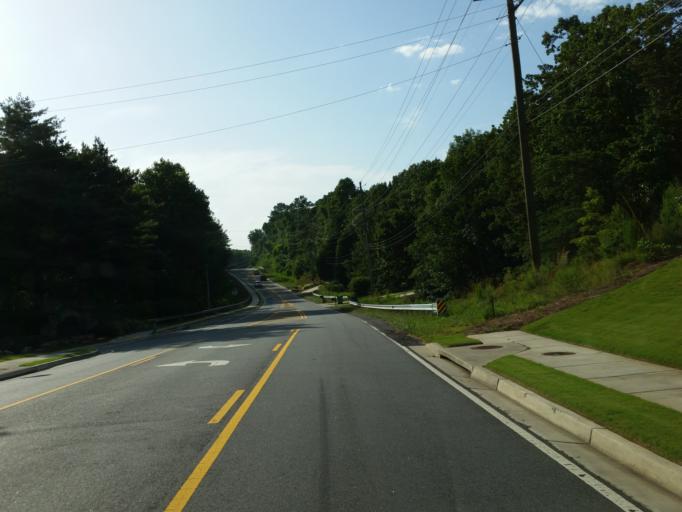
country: US
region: Georgia
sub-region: Cherokee County
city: Woodstock
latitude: 34.0579
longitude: -84.4584
